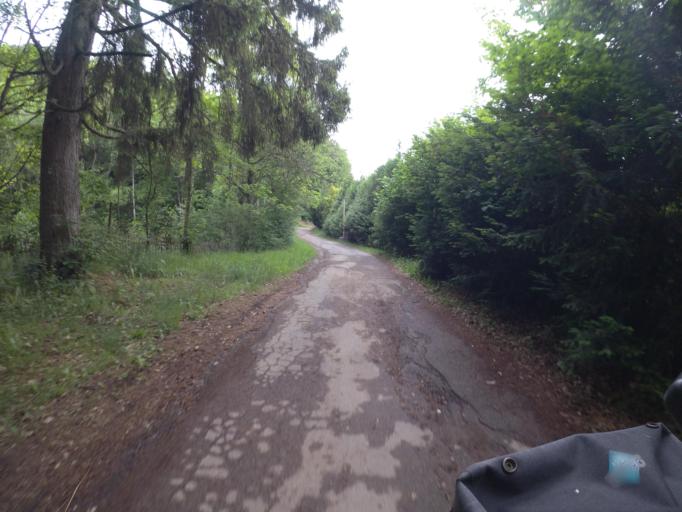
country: DE
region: North Rhine-Westphalia
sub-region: Regierungsbezirk Koln
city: Schleiden
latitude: 50.5104
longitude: 6.4632
